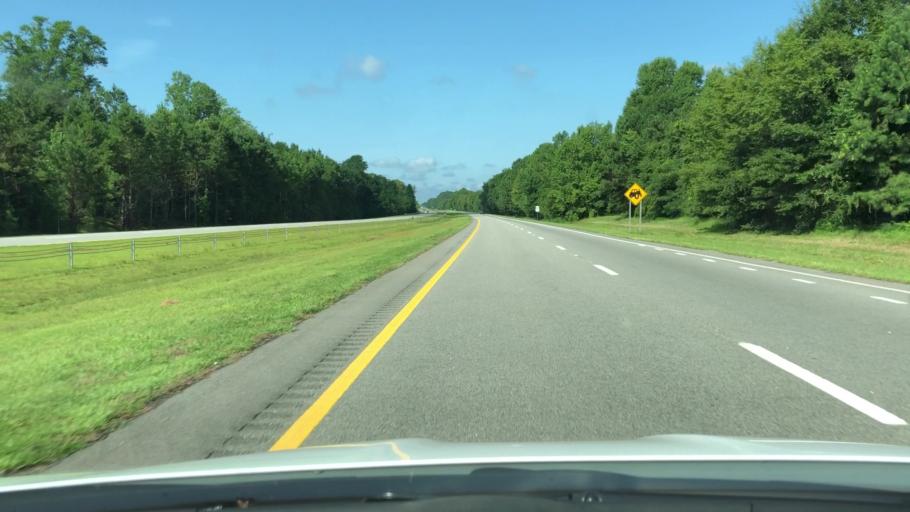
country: US
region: North Carolina
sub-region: Chowan County
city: Edenton
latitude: 36.0686
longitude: -76.6376
